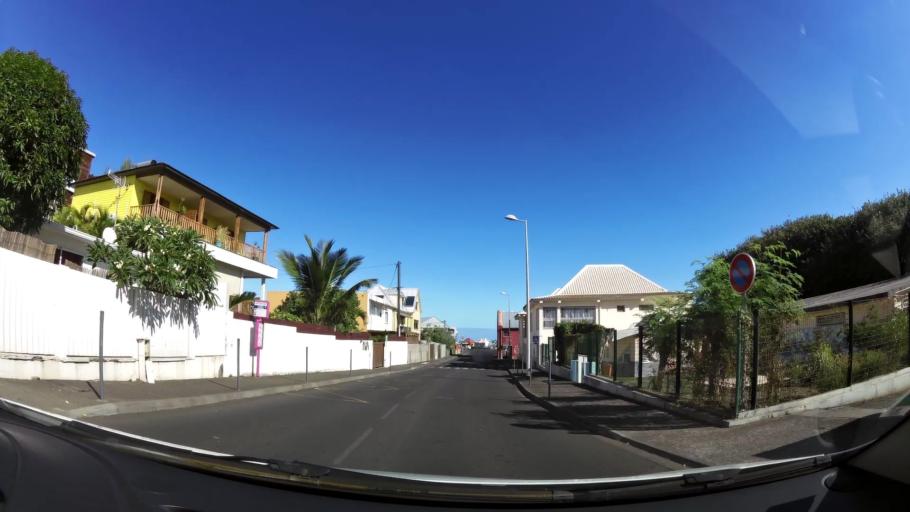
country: RE
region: Reunion
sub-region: Reunion
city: Saint-Pierre
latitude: -21.3428
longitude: 55.4800
